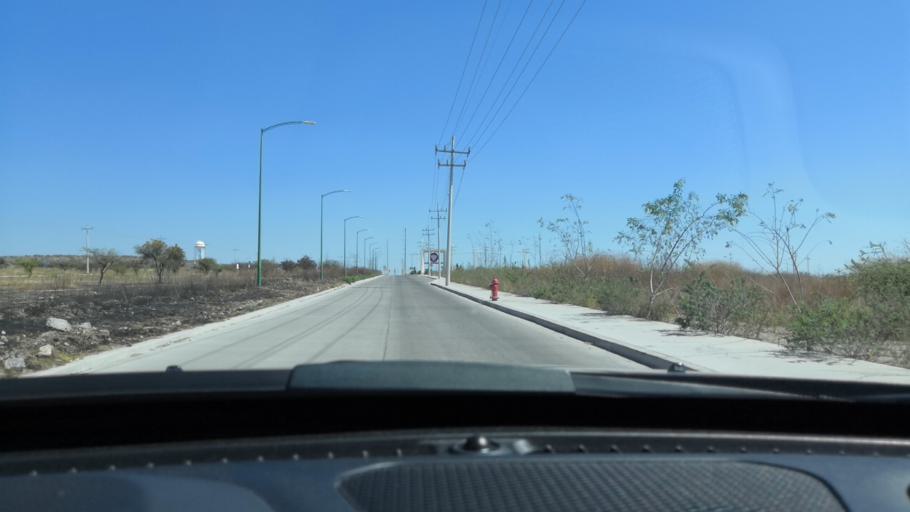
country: MX
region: Guanajuato
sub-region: Leon
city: Centro Familiar la Soledad
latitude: 21.1080
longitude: -101.7617
